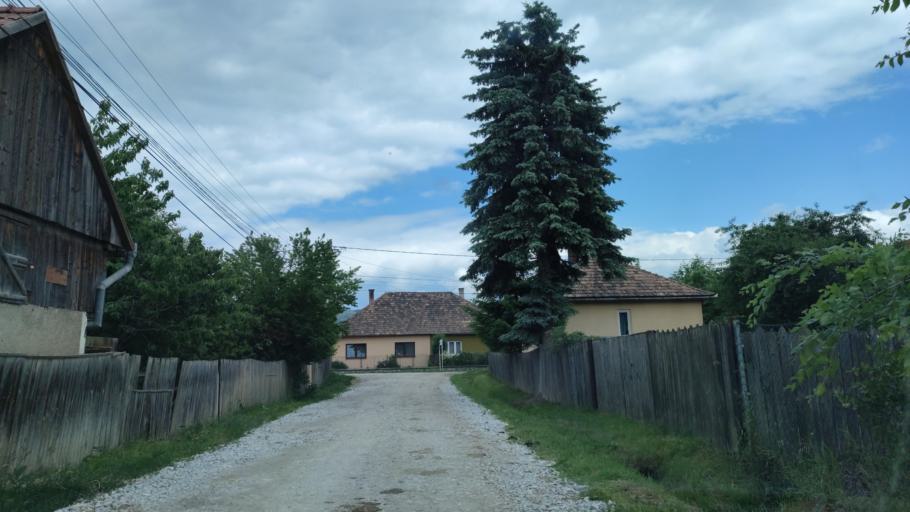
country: RO
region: Harghita
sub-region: Municipiul Gheorgheni
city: Gheorgheni
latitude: 46.7285
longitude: 25.6077
